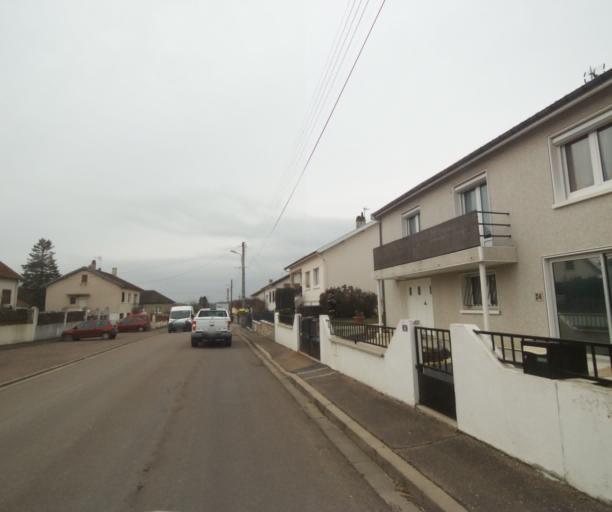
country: FR
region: Champagne-Ardenne
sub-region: Departement de la Haute-Marne
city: Villiers-en-Lieu
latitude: 48.6673
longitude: 4.8963
